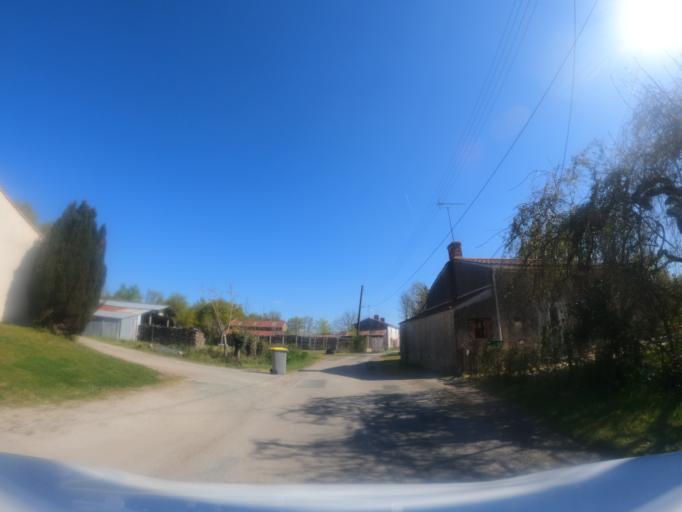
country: FR
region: Pays de la Loire
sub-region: Departement de la Vendee
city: Le Champ-Saint-Pere
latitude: 46.5387
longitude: -1.3569
